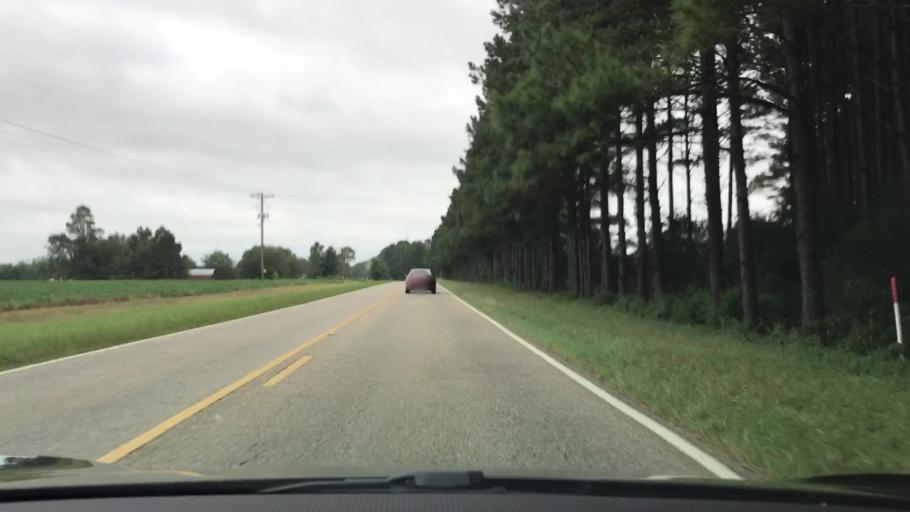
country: US
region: Alabama
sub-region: Geneva County
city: Samson
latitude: 31.1581
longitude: -86.1416
